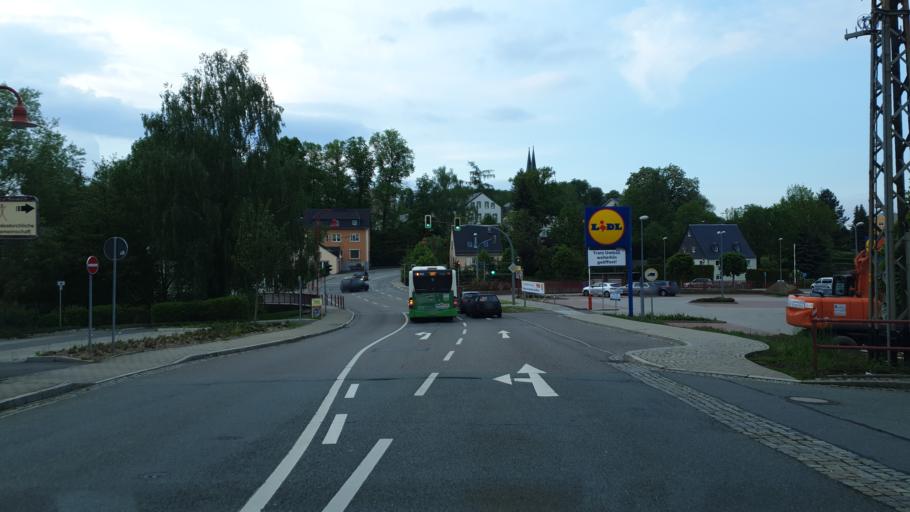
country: DE
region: Saxony
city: Lugau
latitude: 50.7205
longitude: 12.7552
